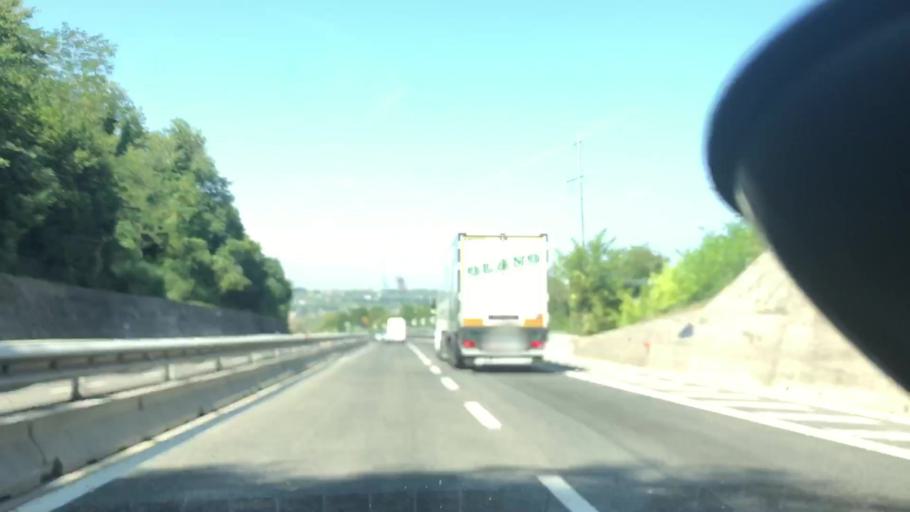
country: IT
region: Abruzzo
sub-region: Provincia di Chieti
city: Tollo
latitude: 42.3704
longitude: 14.3166
